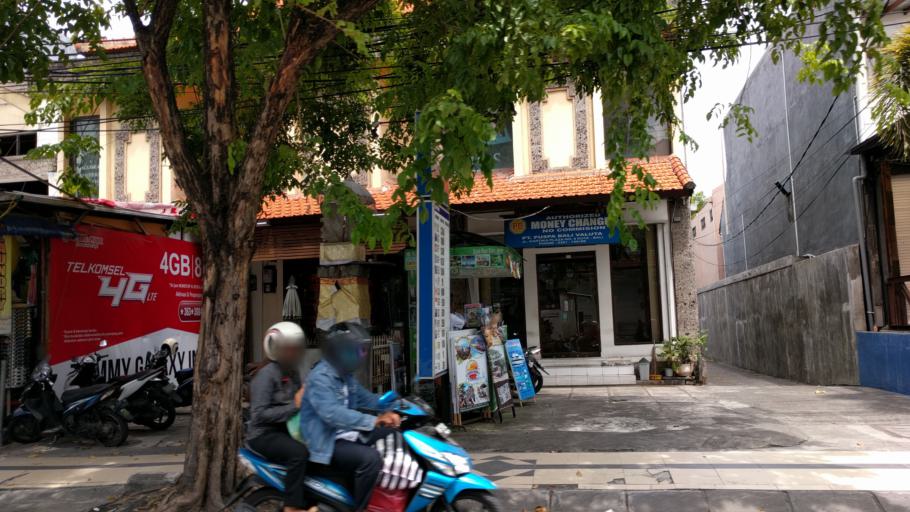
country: ID
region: Bali
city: Jabajero
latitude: -8.7362
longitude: 115.1673
